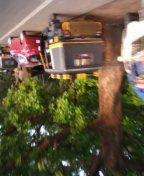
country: IN
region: Kerala
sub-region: Thrissur District
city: Trichur
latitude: 10.5383
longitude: 76.1844
